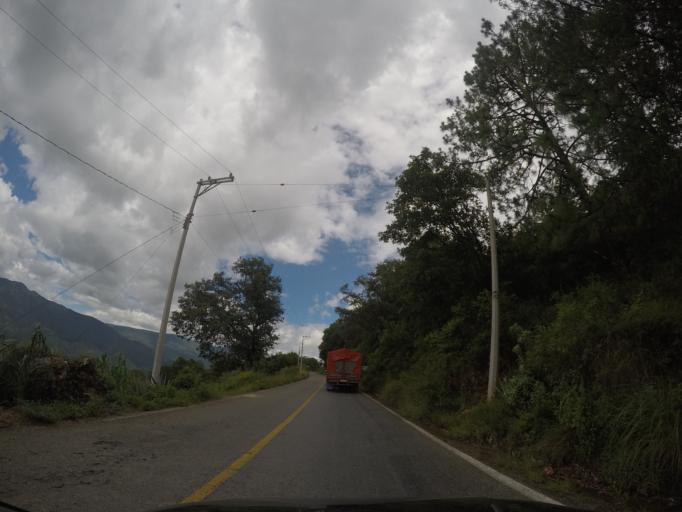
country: MX
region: Oaxaca
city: San Francisco Sola
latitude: 16.4846
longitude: -96.9826
